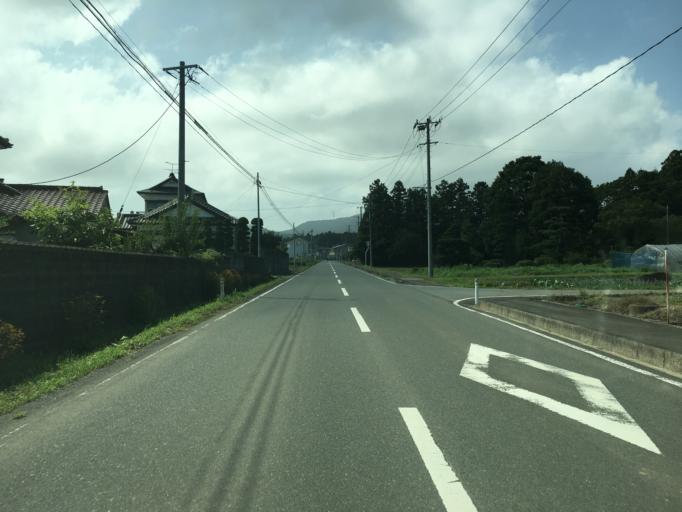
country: JP
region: Miyagi
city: Marumori
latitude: 37.8406
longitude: 140.8961
